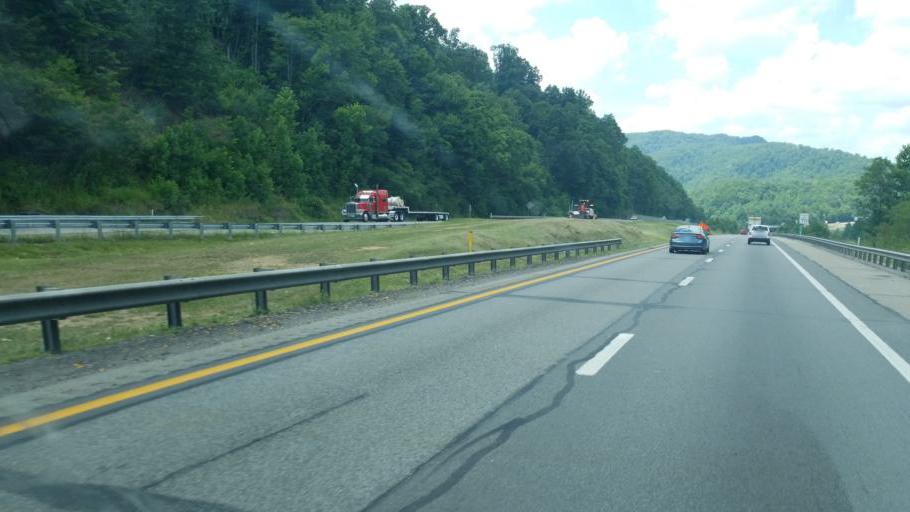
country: US
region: West Virginia
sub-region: Raleigh County
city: Bradley
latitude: 37.8730
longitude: -81.2627
